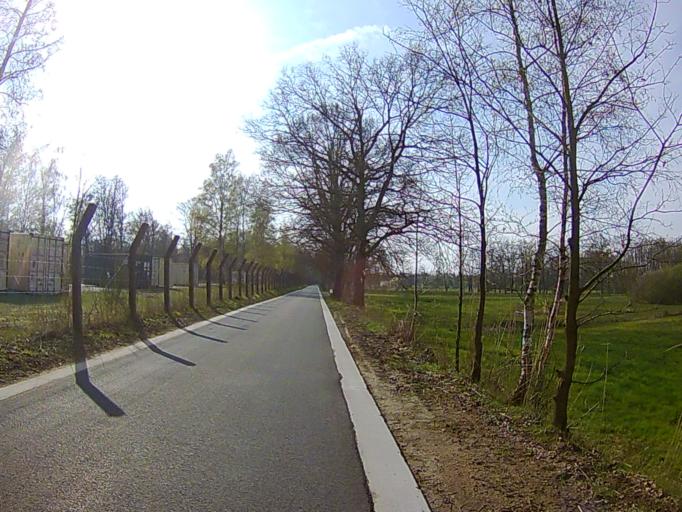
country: BE
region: Flanders
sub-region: Provincie Antwerpen
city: Vorselaar
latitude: 51.1859
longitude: 4.7632
